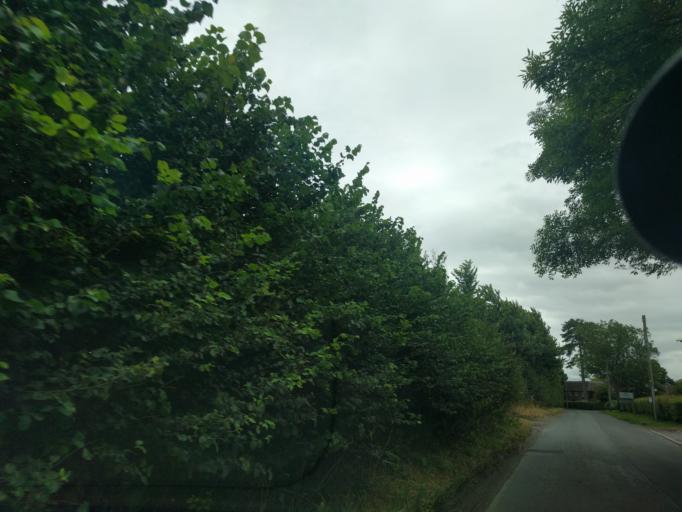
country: GB
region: England
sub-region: Wiltshire
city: Market Lavington
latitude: 51.2817
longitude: -2.0064
